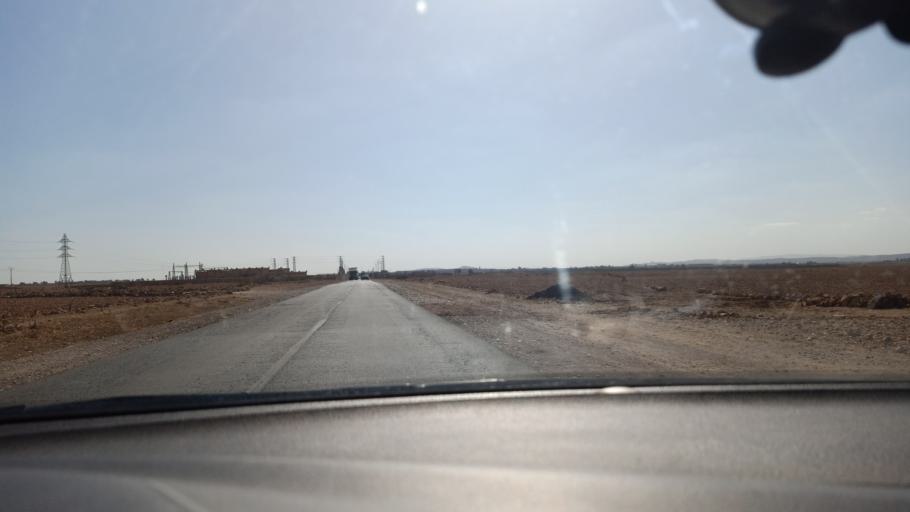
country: MA
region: Doukkala-Abda
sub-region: Safi
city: Youssoufia
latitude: 32.1135
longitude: -8.6071
